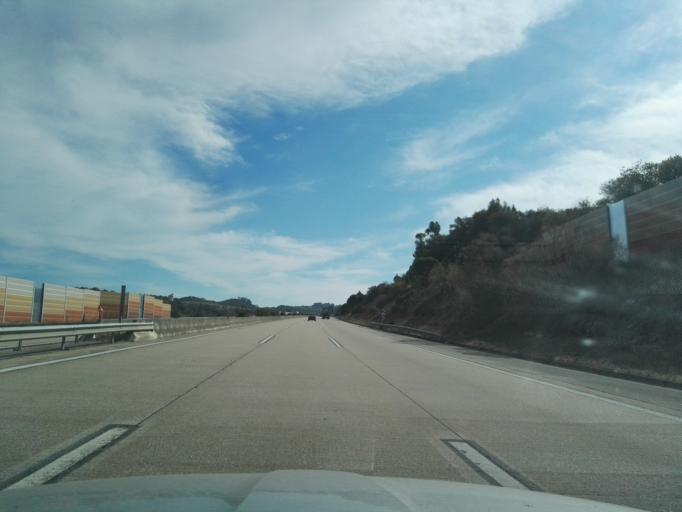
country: PT
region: Lisbon
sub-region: Loures
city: Bucelas
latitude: 38.9002
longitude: -9.1042
